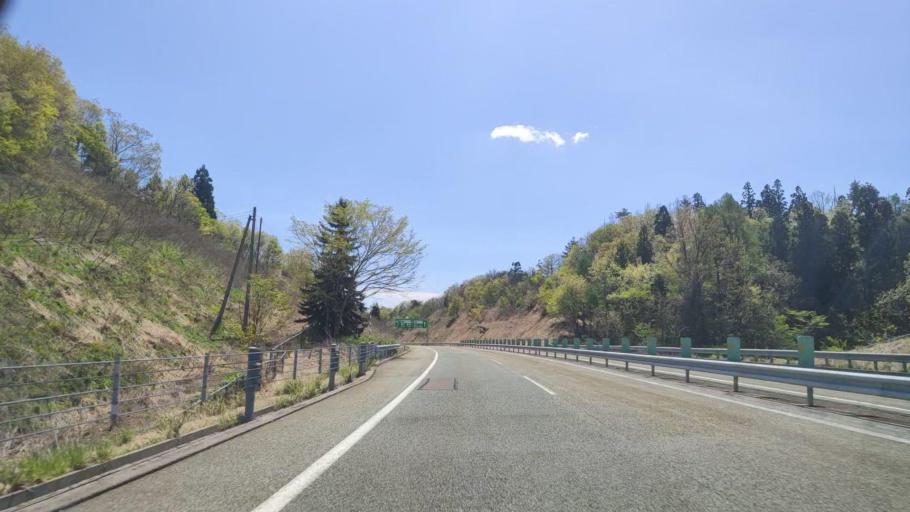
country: JP
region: Akita
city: Yokotemachi
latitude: 39.2844
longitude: 140.5314
